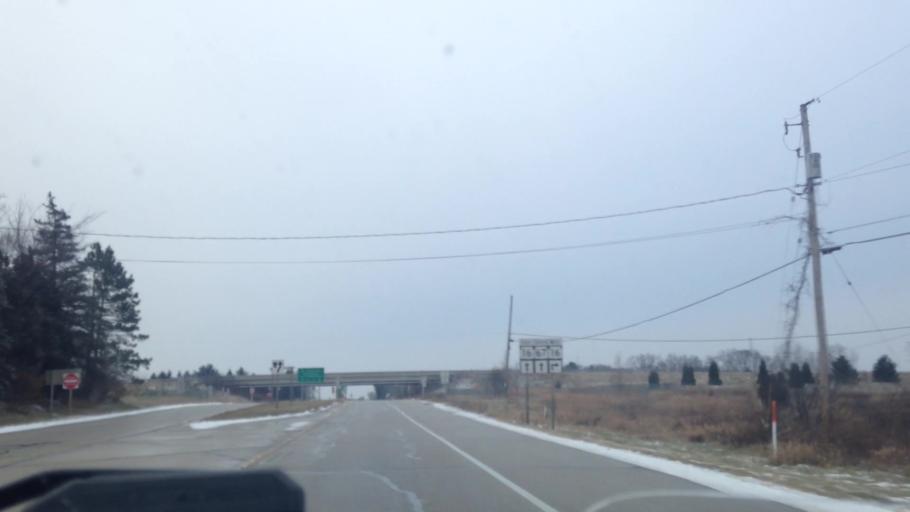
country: US
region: Wisconsin
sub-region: Waukesha County
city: Oconomowoc
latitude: 43.1513
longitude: -88.4998
